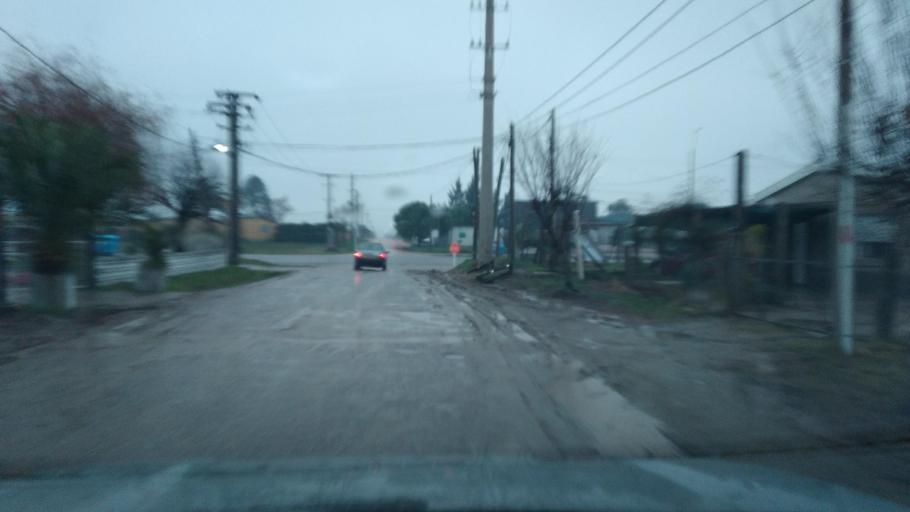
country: UY
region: Florida
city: Florida
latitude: -34.0789
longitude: -56.2231
